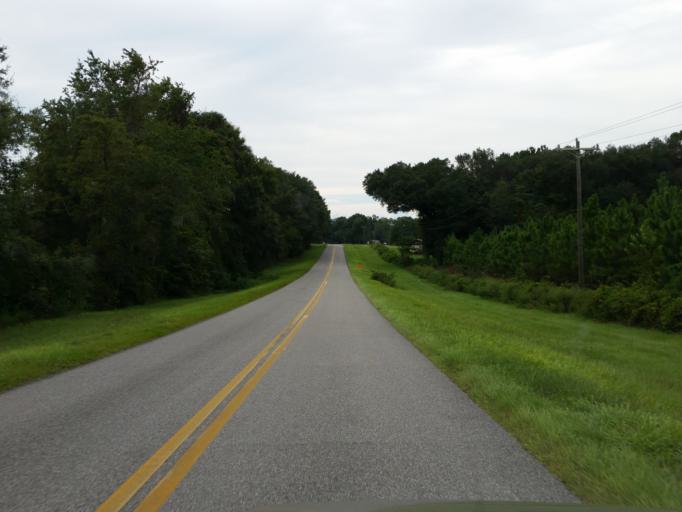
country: US
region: Florida
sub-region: Alachua County
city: High Springs
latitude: 29.9514
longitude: -82.5102
